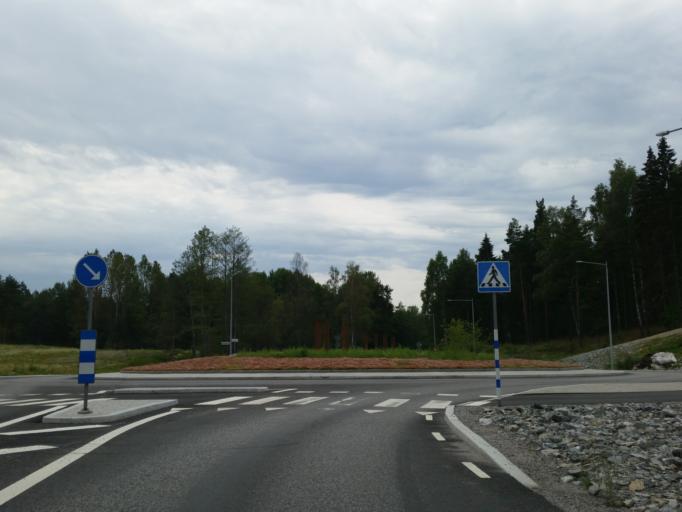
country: SE
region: Stockholm
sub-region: Sodertalje Kommun
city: Soedertaelje
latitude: 59.2135
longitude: 17.6544
